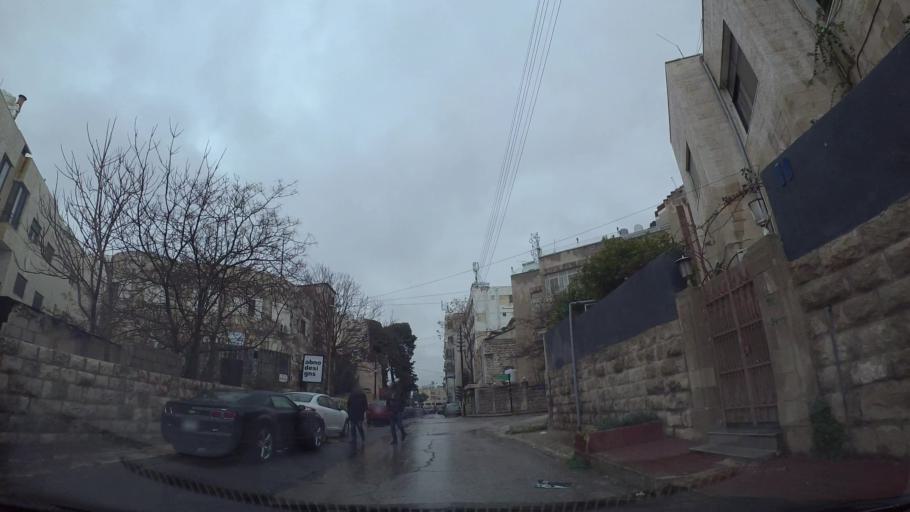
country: JO
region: Amman
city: Amman
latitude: 31.9572
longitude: 35.9274
